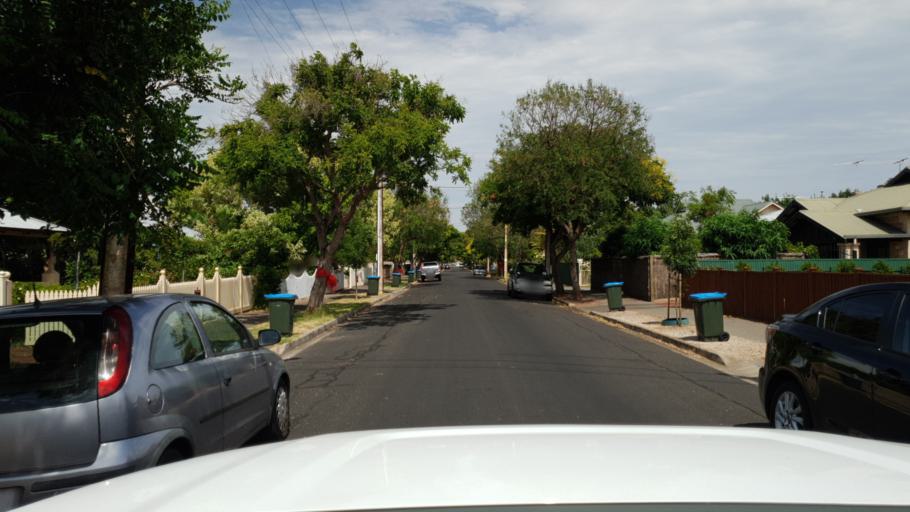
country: AU
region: South Australia
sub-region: Mitcham
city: Clarence Gardens
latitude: -34.9734
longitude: 138.5862
